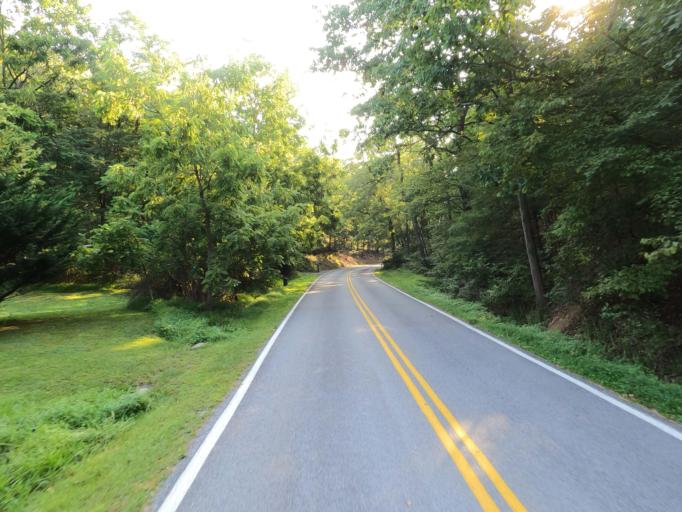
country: US
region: West Virginia
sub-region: Morgan County
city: Berkeley Springs
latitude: 39.6769
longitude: -78.2737
